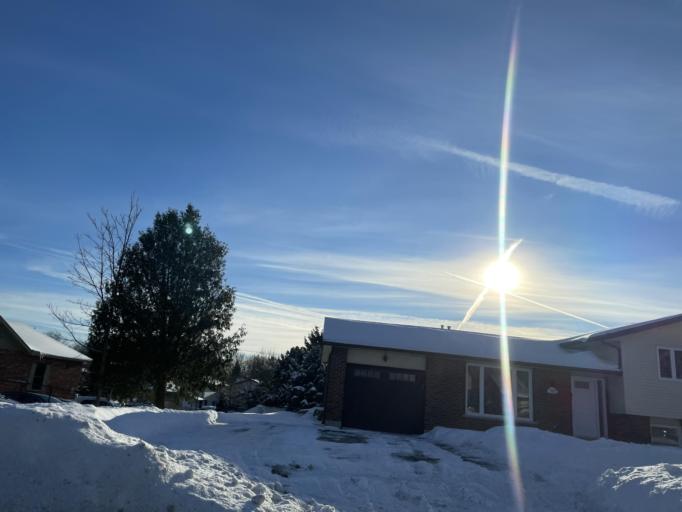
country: CA
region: Ontario
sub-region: Wellington County
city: Guelph
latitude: 43.5111
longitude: -80.2291
